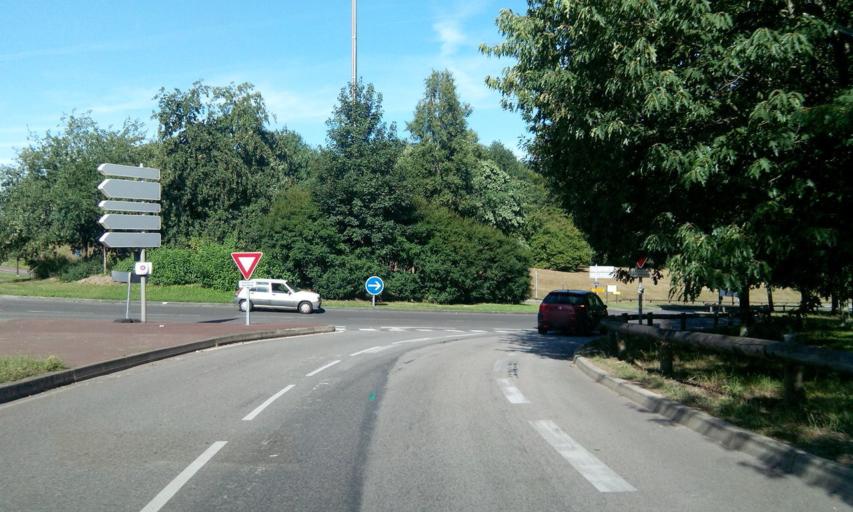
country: FR
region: Limousin
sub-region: Departement de la Haute-Vienne
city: Limoges
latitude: 45.8615
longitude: 1.2757
